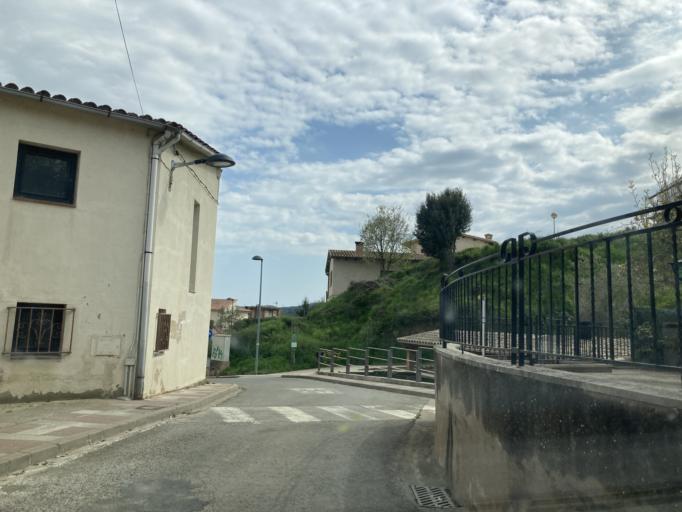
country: ES
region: Catalonia
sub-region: Provincia de Girona
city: la Cellera de Ter
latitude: 41.9696
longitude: 2.6185
